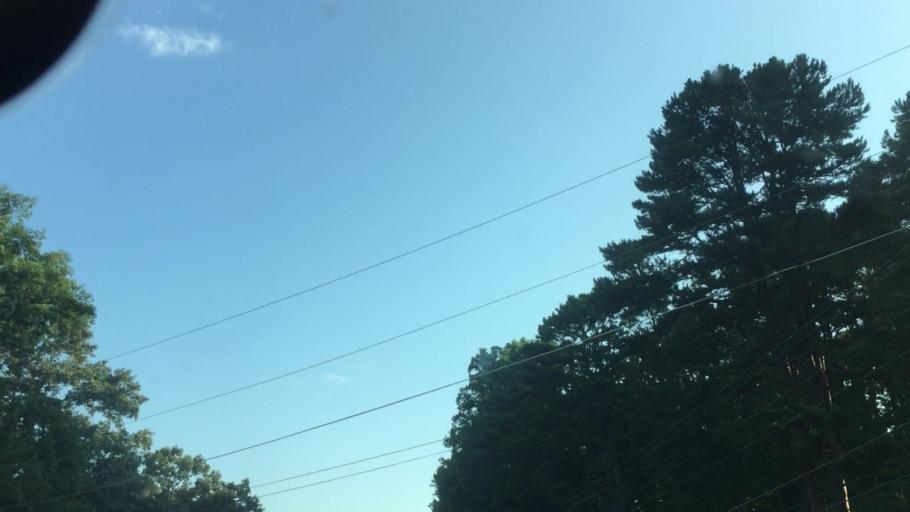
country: US
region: Georgia
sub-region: DeKalb County
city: Pine Mountain
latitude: 33.6742
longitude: -84.1958
